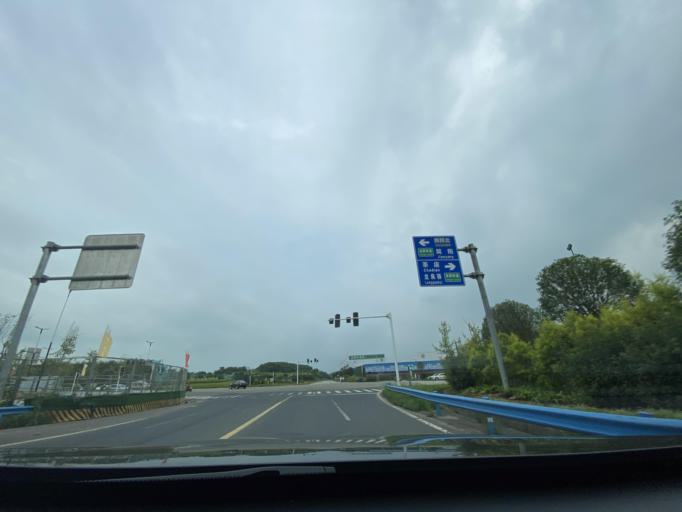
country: CN
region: Sichuan
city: Jiancheng
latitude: 30.4952
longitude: 104.4500
